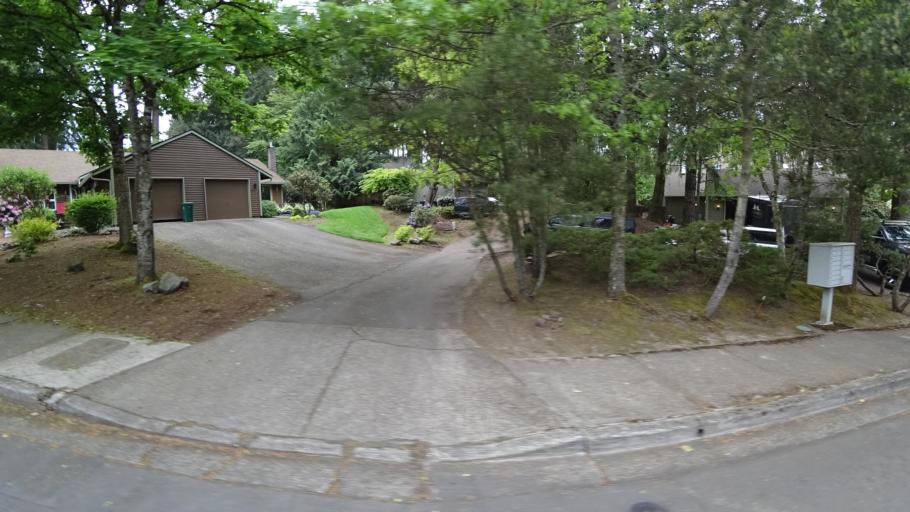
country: US
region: Oregon
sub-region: Washington County
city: Beaverton
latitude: 45.4832
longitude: -122.8347
